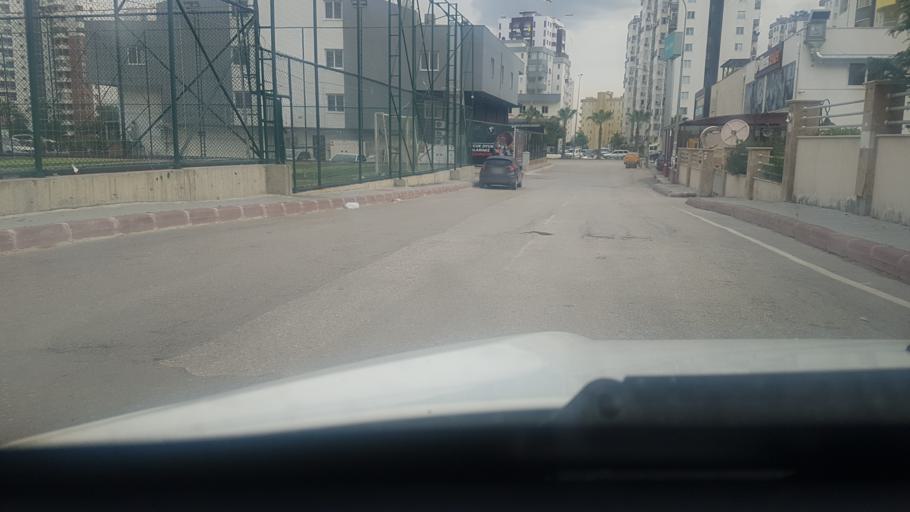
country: TR
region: Adana
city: Seyhan
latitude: 37.0228
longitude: 35.2770
